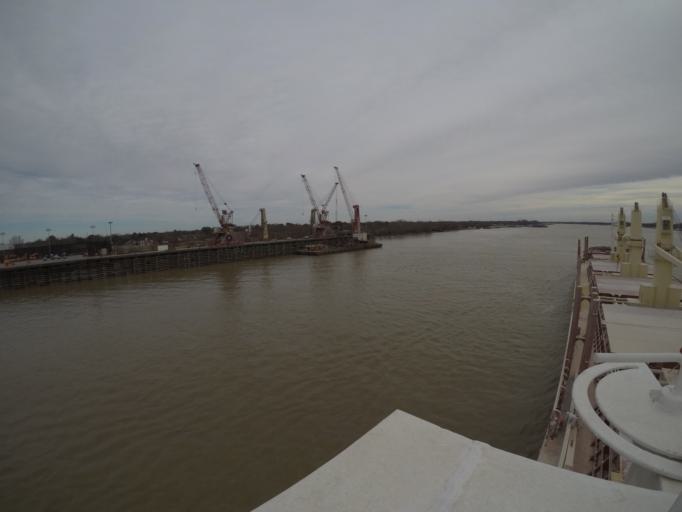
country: US
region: Louisiana
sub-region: Saint John the Baptist Parish
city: Edgard
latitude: 30.0520
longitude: -90.5645
